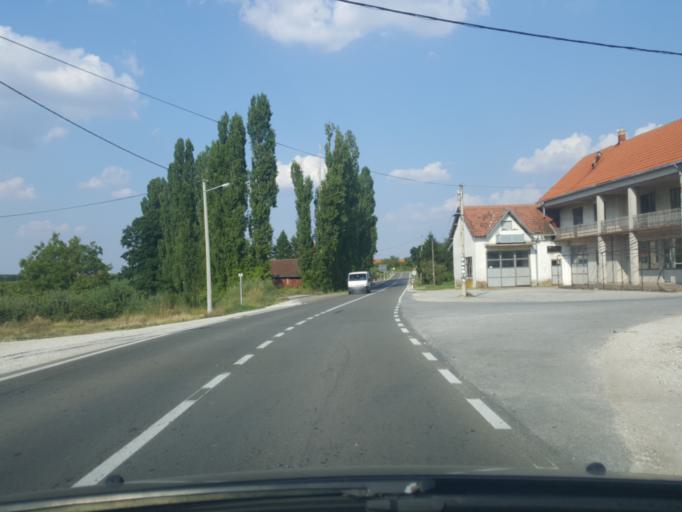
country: RS
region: Central Serbia
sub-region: Sumadijski Okrug
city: Topola
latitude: 44.2196
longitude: 20.6210
